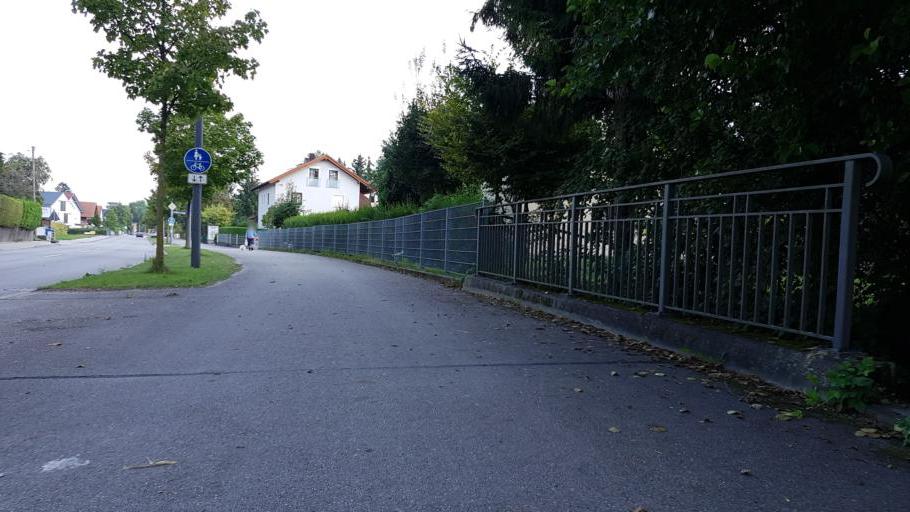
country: DE
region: Bavaria
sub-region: Upper Bavaria
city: Karlsfeld
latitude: 48.2181
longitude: 11.5206
